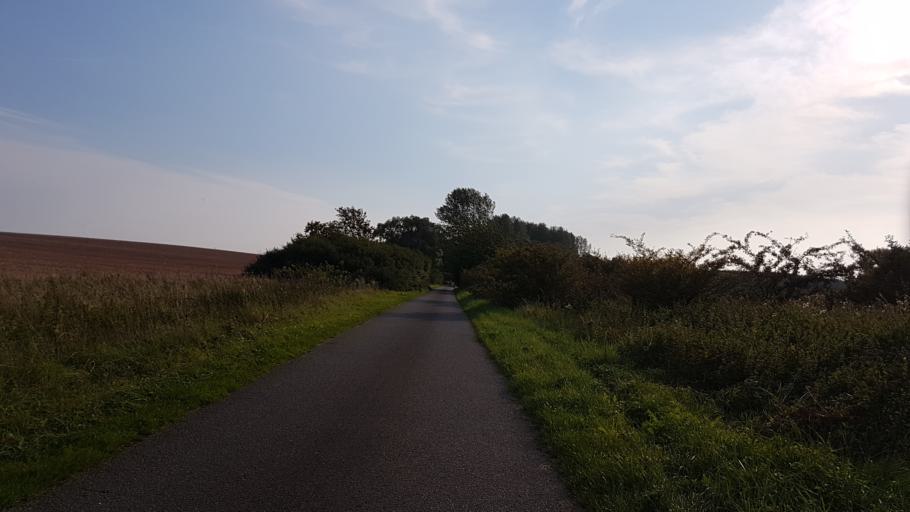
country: DE
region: Mecklenburg-Vorpommern
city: Sagard
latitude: 54.5129
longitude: 13.5289
